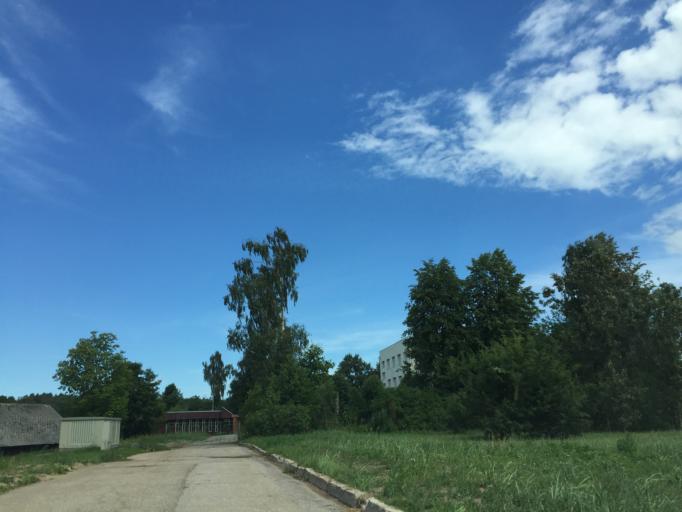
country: LV
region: Saulkrastu
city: Saulkrasti
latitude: 57.3168
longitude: 24.4129
